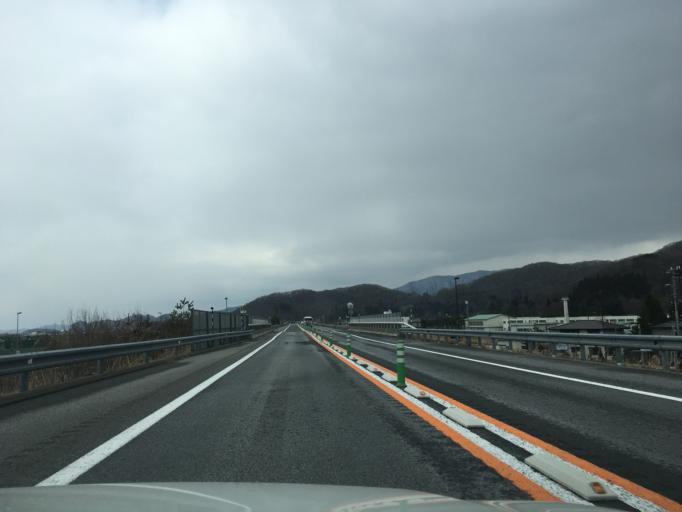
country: JP
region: Aomori
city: Aomori Shi
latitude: 40.8075
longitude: 140.7987
